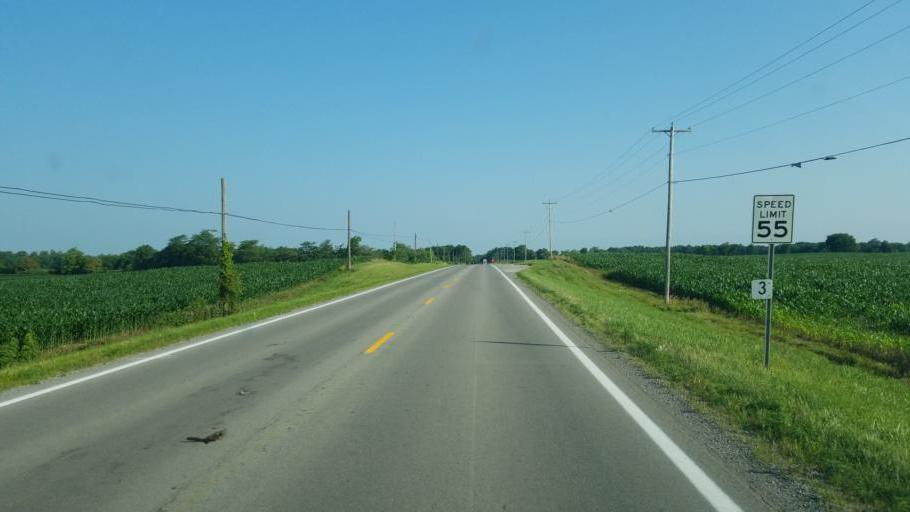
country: US
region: Ohio
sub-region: Hardin County
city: Kenton
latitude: 40.5418
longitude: -83.5258
